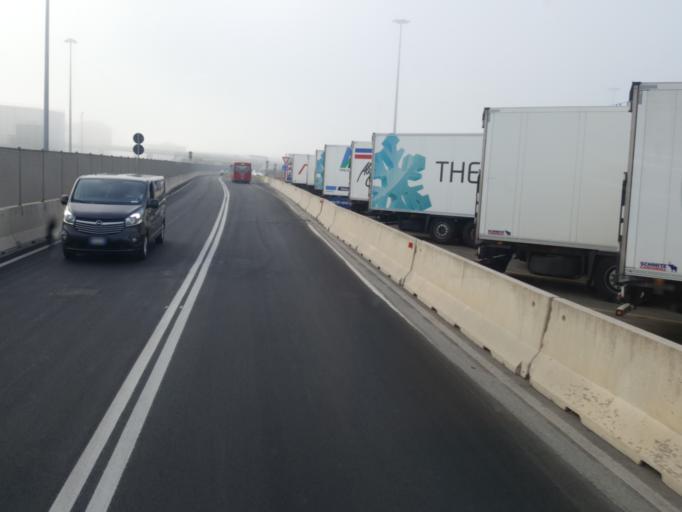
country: IT
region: Latium
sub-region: Citta metropolitana di Roma Capitale
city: Civitavecchia
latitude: 42.1049
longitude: 11.7799
